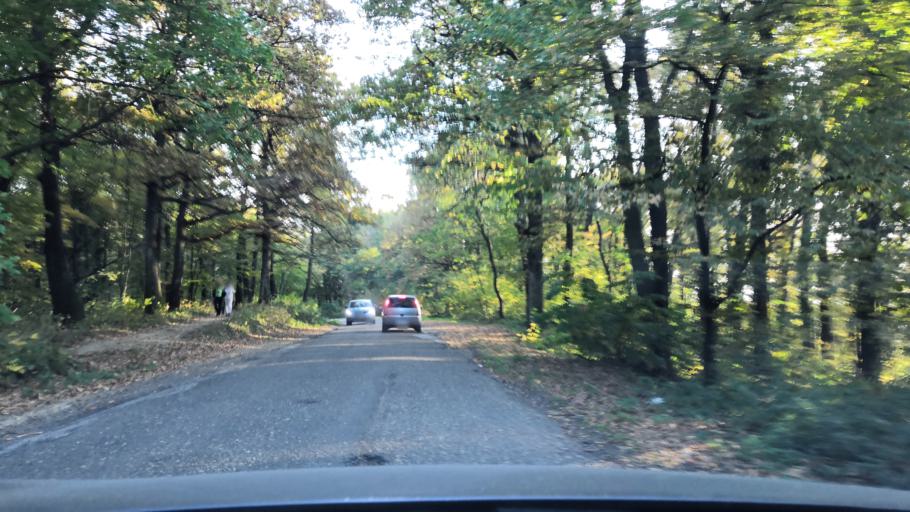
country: RS
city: Vrdnik
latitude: 45.1516
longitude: 19.8231
